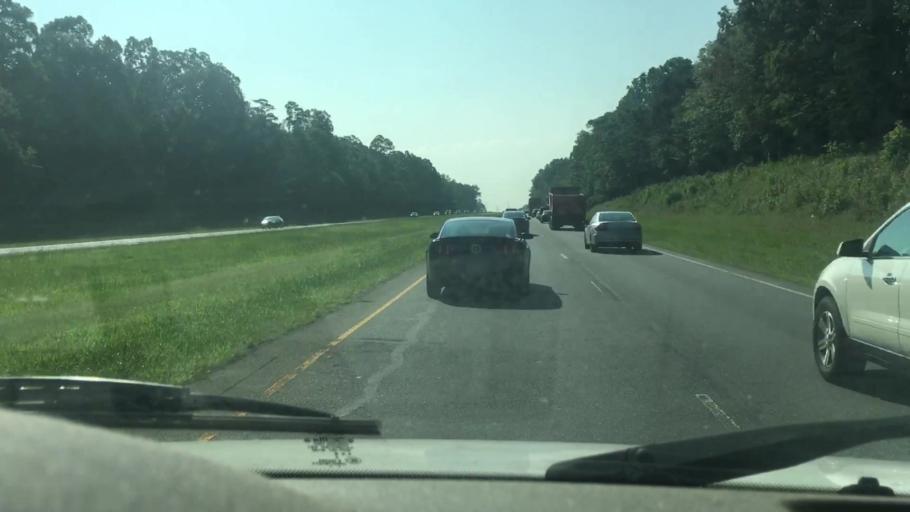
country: US
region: North Carolina
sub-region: Gaston County
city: Mount Holly
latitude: 35.3375
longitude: -80.9622
